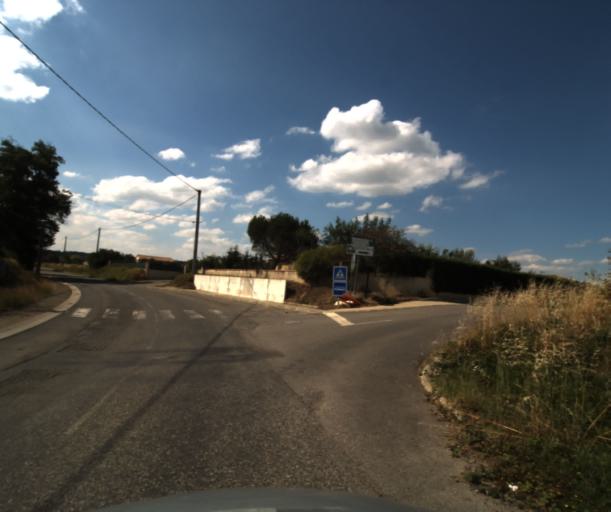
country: FR
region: Midi-Pyrenees
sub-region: Departement de la Haute-Garonne
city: Saint-Lys
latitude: 43.5222
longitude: 1.1637
